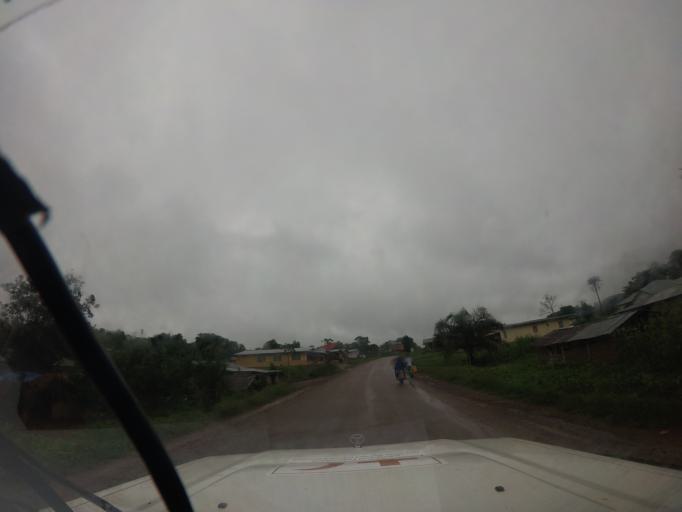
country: SL
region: Northern Province
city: Kabala
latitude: 9.5473
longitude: -11.5688
